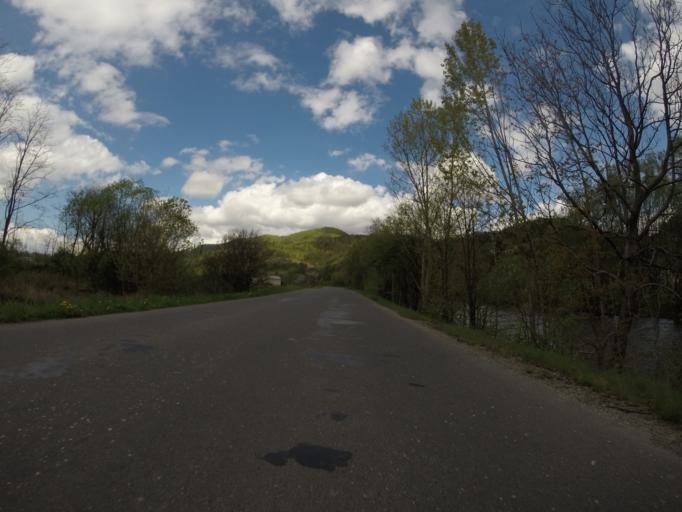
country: SK
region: Banskobystricky
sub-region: Okres Banska Bystrica
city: Brezno
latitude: 48.8146
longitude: 19.4376
